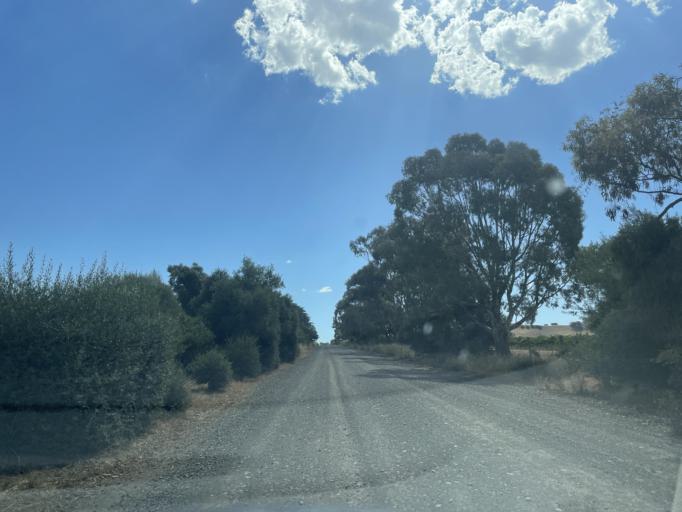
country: AU
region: South Australia
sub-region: Clare and Gilbert Valleys
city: Clare
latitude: -33.9119
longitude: 138.7208
